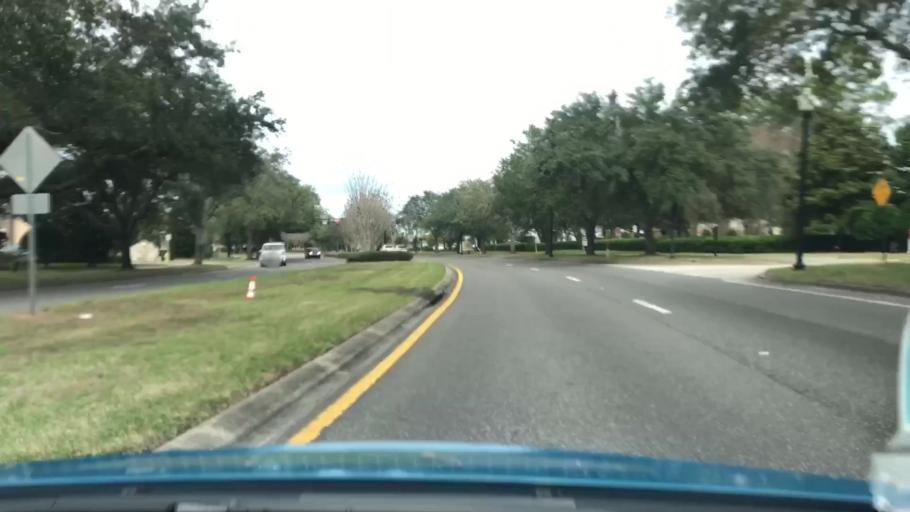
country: US
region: Florida
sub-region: Seminole County
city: Heathrow
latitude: 28.7793
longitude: -81.3573
